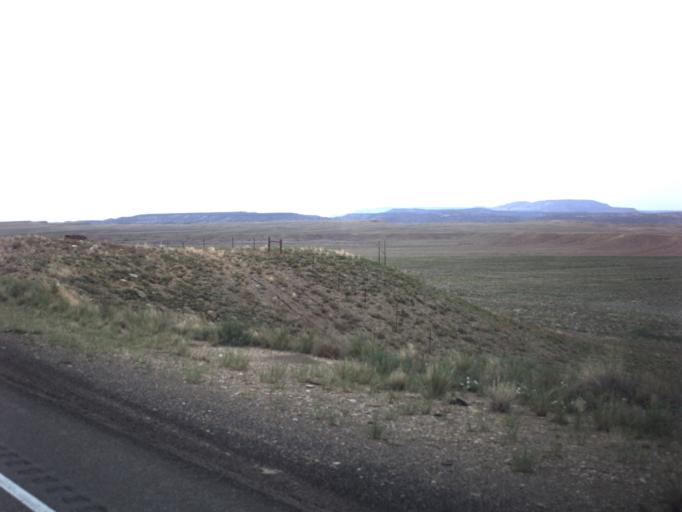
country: US
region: Utah
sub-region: Carbon County
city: East Carbon City
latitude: 39.4880
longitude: -110.5164
